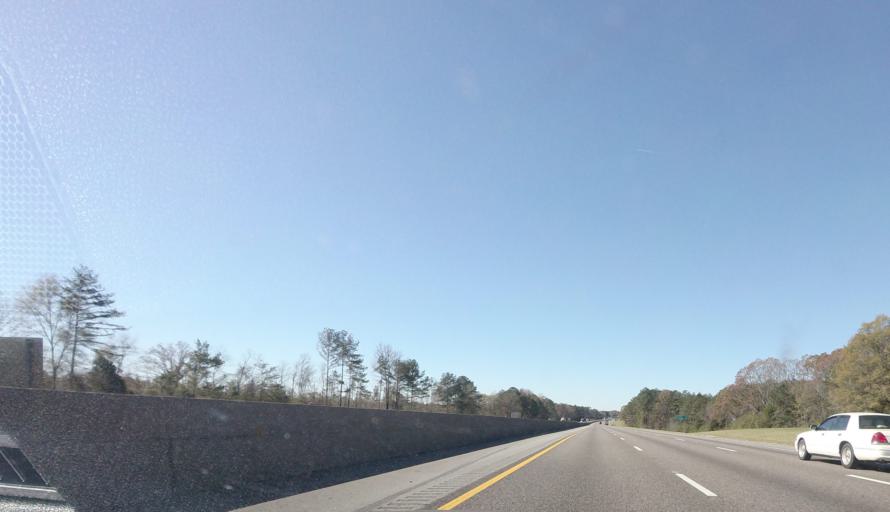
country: US
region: Alabama
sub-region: Calhoun County
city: Bynum
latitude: 33.5827
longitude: -85.9358
